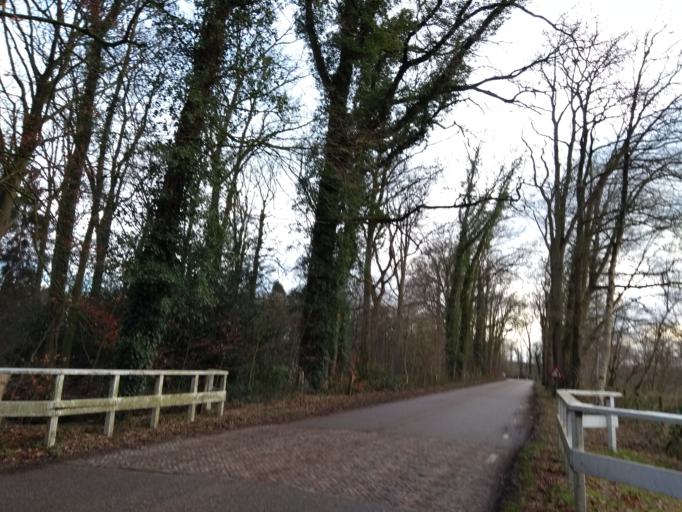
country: NL
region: Overijssel
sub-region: Gemeente Enschede
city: Enschede
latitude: 52.2550
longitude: 6.8812
